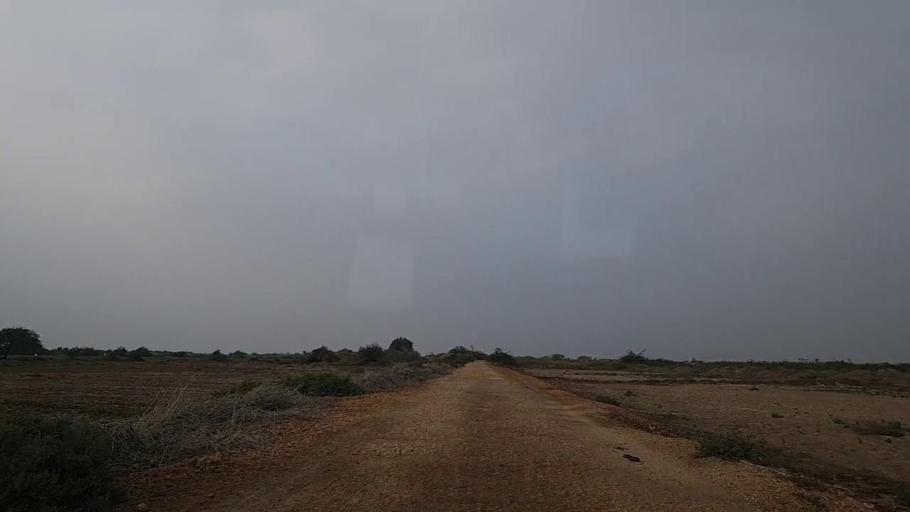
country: PK
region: Sindh
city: Mirpur Sakro
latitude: 24.6077
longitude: 67.5159
